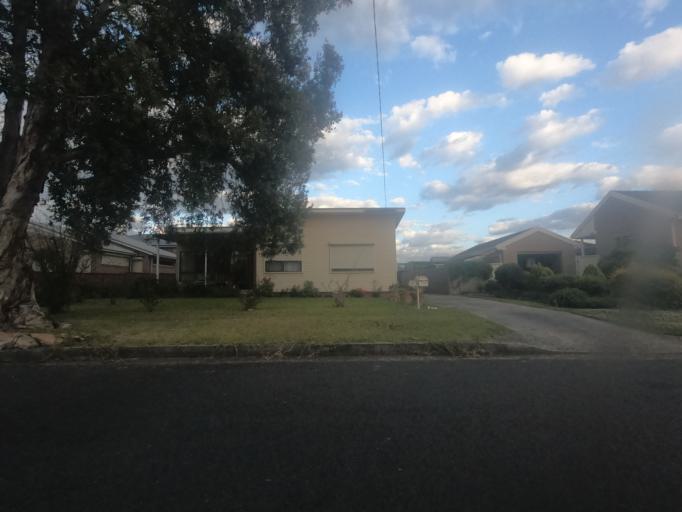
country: AU
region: New South Wales
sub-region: Wollongong
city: Koonawarra
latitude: -34.4992
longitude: 150.8010
